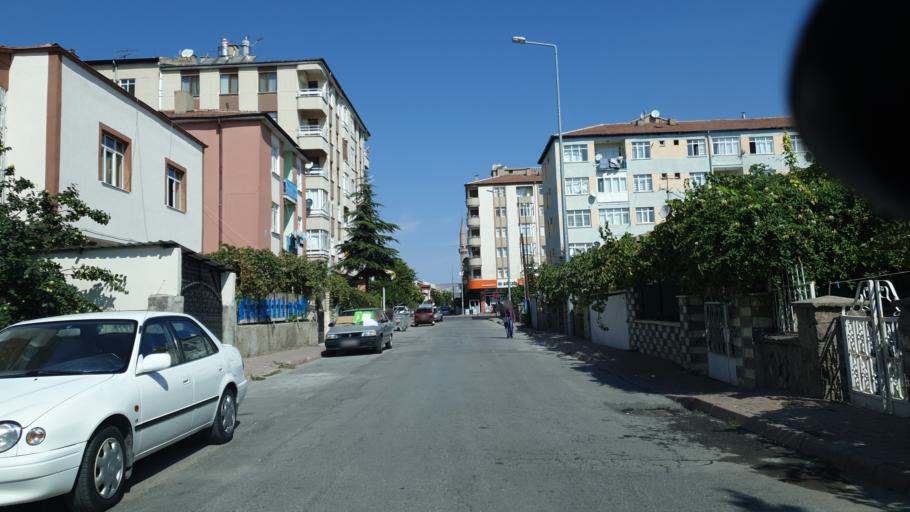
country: TR
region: Kayseri
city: Kayseri
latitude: 38.7379
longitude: 35.4892
